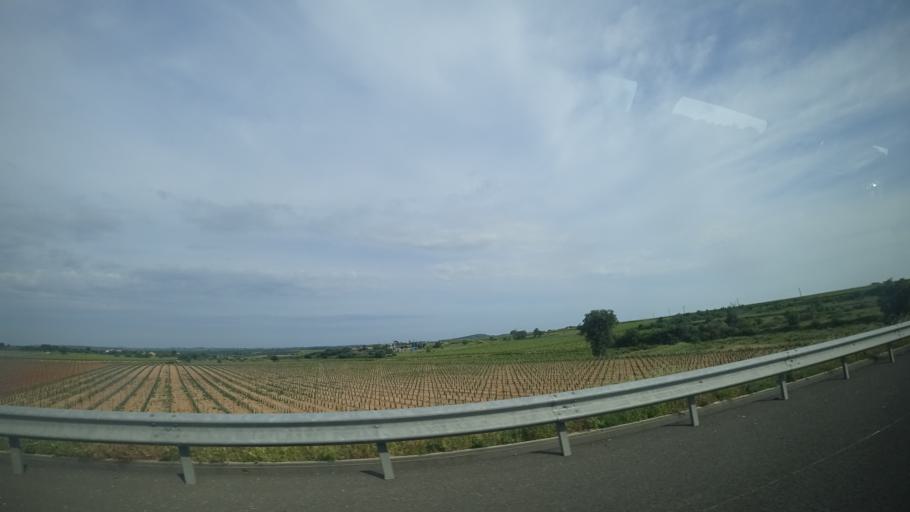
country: FR
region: Languedoc-Roussillon
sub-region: Departement de l'Herault
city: Valros
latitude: 43.4170
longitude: 3.3837
